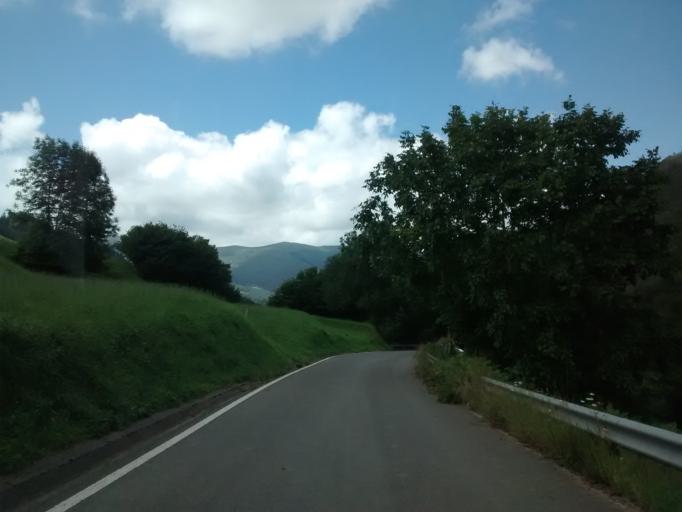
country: ES
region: Cantabria
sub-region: Provincia de Cantabria
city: Ruente
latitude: 43.1914
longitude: -4.2676
